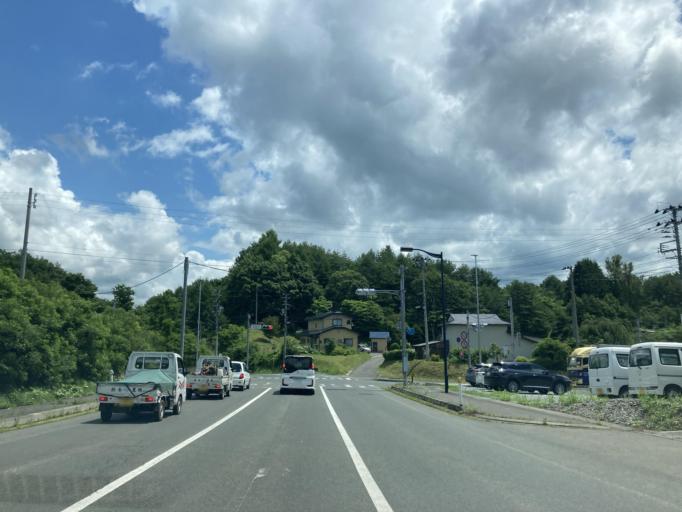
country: JP
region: Iwate
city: Ichinohe
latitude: 39.9732
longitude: 141.2142
